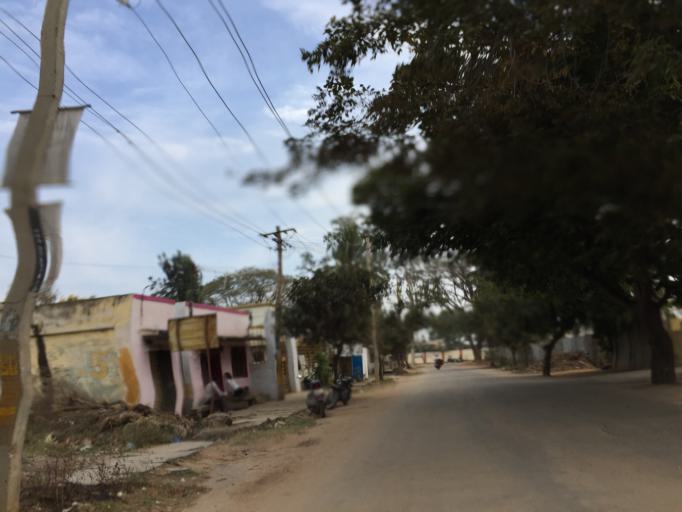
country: IN
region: Karnataka
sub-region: Kolar
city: Kolar
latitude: 13.1299
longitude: 78.1194
